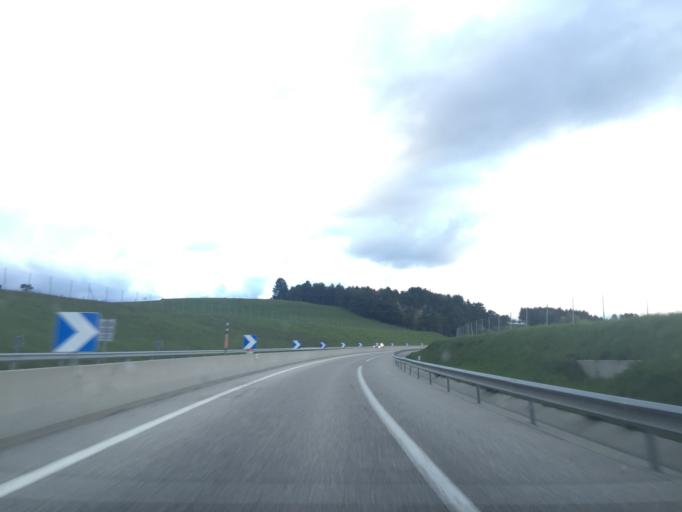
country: FR
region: Rhone-Alpes
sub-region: Departement de l'Isere
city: La Motte-Saint-Martin
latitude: 44.9146
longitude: 5.6232
